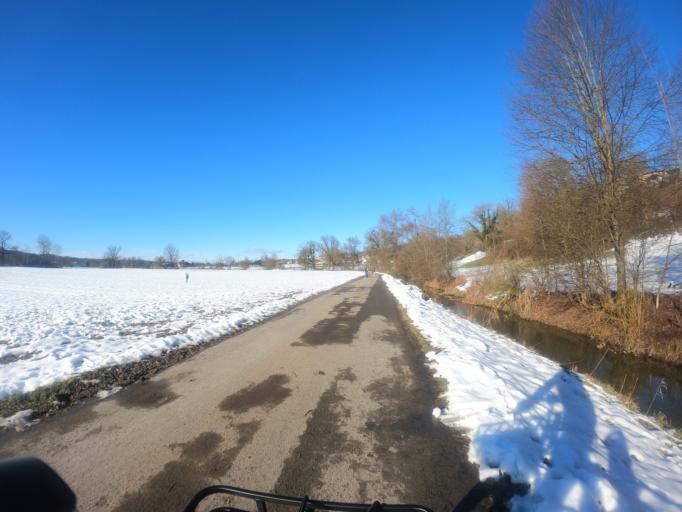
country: CH
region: Aargau
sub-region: Bezirk Bremgarten
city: Oberlunkhofen
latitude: 47.3144
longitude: 8.3845
